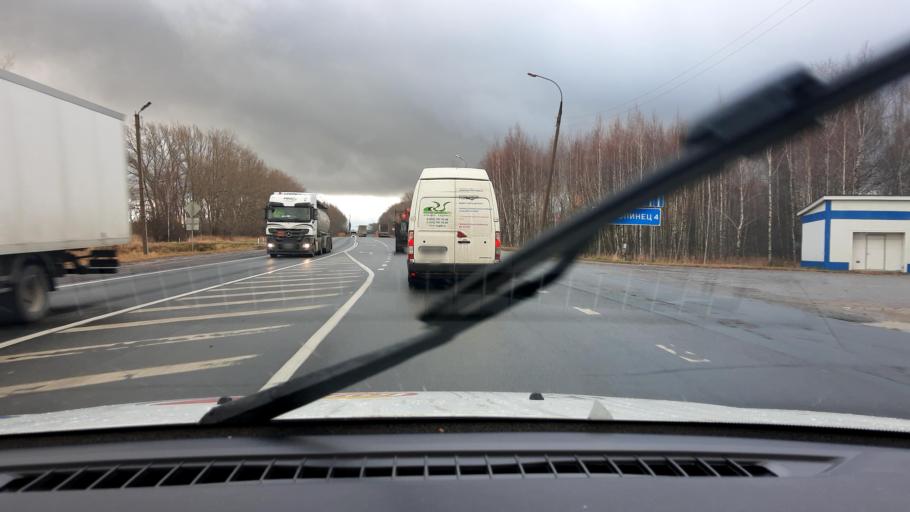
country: RU
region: Nizjnij Novgorod
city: Pamyat' Parizhskoy Kommuny
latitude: 56.0049
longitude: 44.6305
